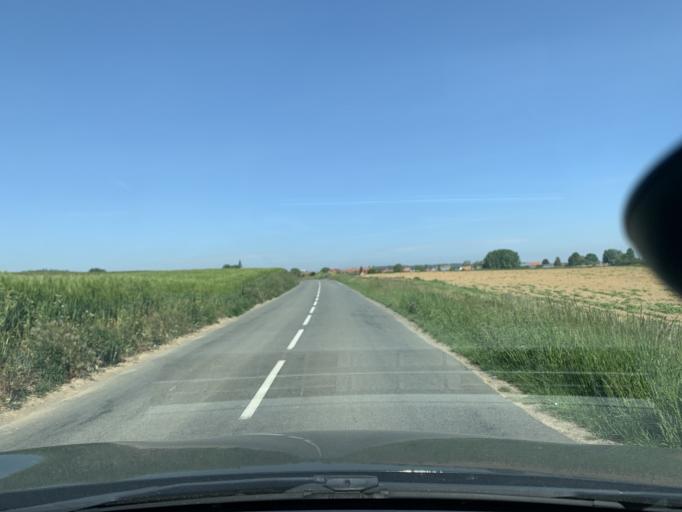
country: FR
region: Nord-Pas-de-Calais
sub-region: Departement du Nord
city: Marcoing
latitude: 50.1442
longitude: 3.1713
